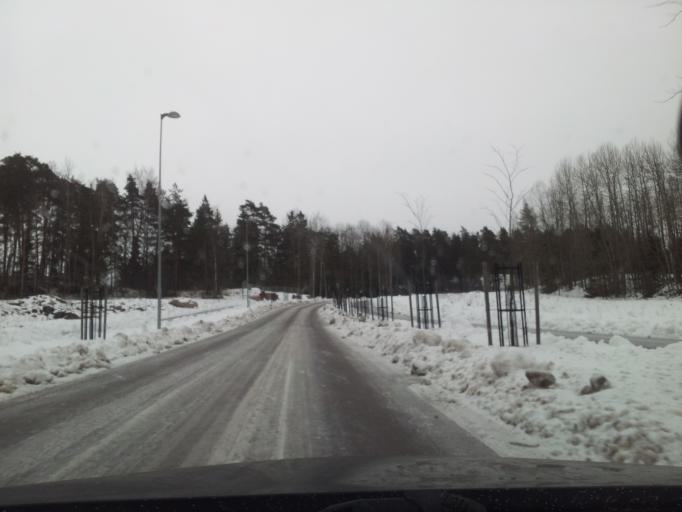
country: FI
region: Uusimaa
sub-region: Helsinki
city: Espoo
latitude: 60.1601
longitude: 24.5564
